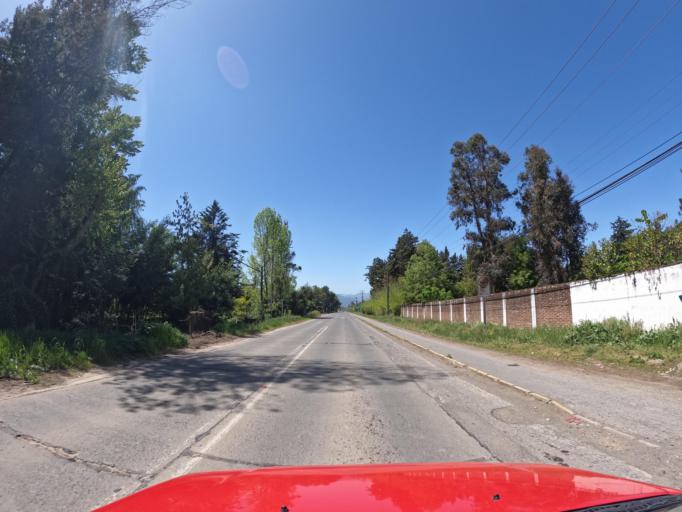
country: CL
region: Maule
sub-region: Provincia de Linares
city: Linares
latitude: -35.8312
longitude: -71.5204
